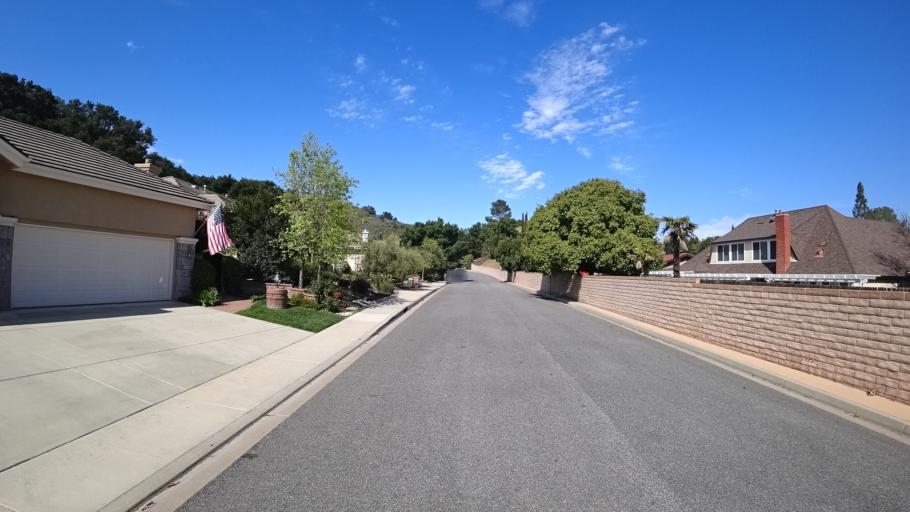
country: US
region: California
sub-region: Ventura County
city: Casa Conejo
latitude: 34.1766
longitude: -118.9275
